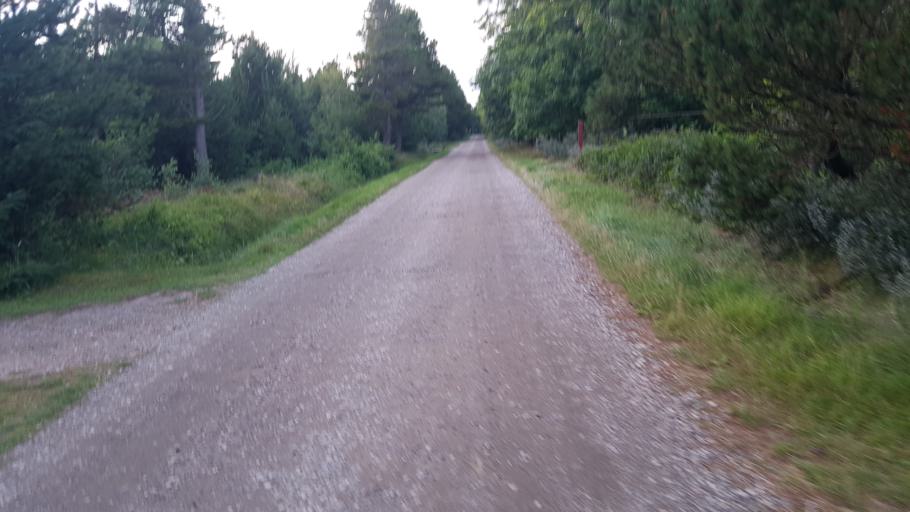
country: DE
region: Schleswig-Holstein
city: List
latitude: 55.0925
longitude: 8.5259
